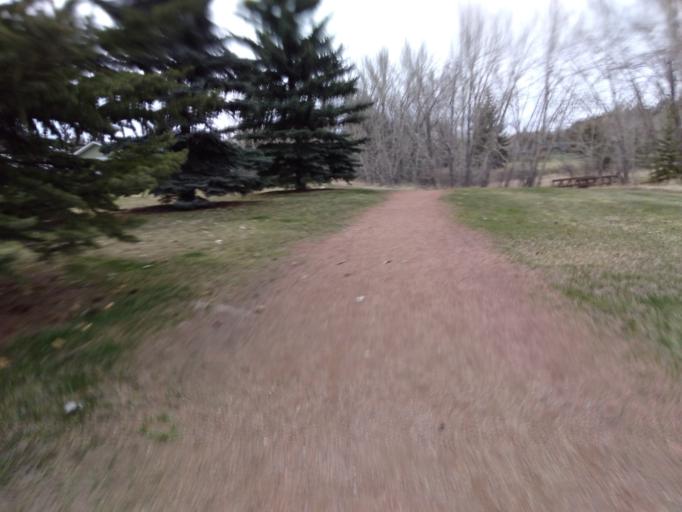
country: CA
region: Alberta
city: Cochrane
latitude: 51.1901
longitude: -114.4810
